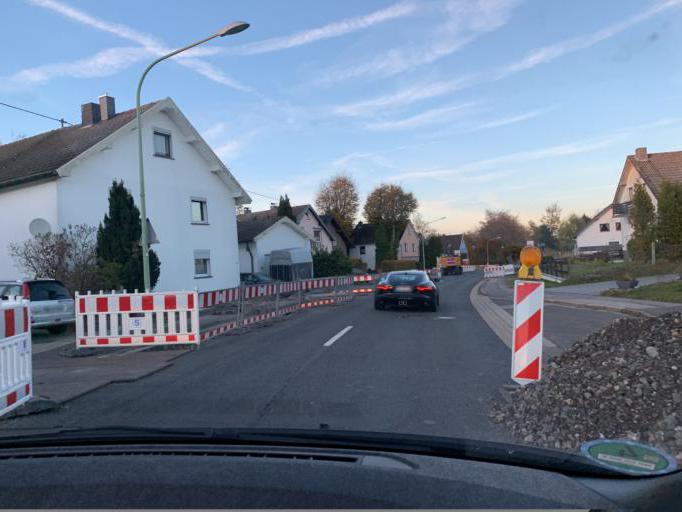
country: DE
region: North Rhine-Westphalia
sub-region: Regierungsbezirk Koln
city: Simmerath
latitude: 50.6310
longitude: 6.3390
